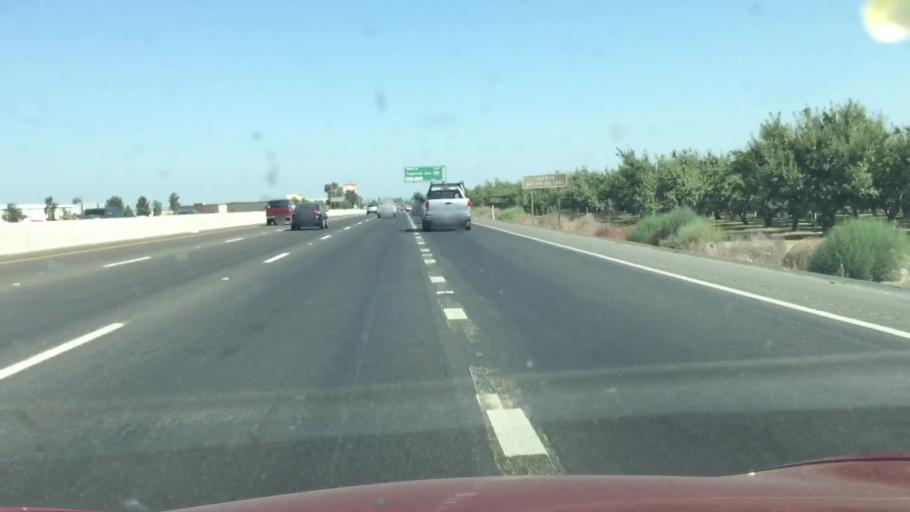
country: US
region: California
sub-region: San Joaquin County
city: Manteca
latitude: 37.7866
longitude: -121.1884
